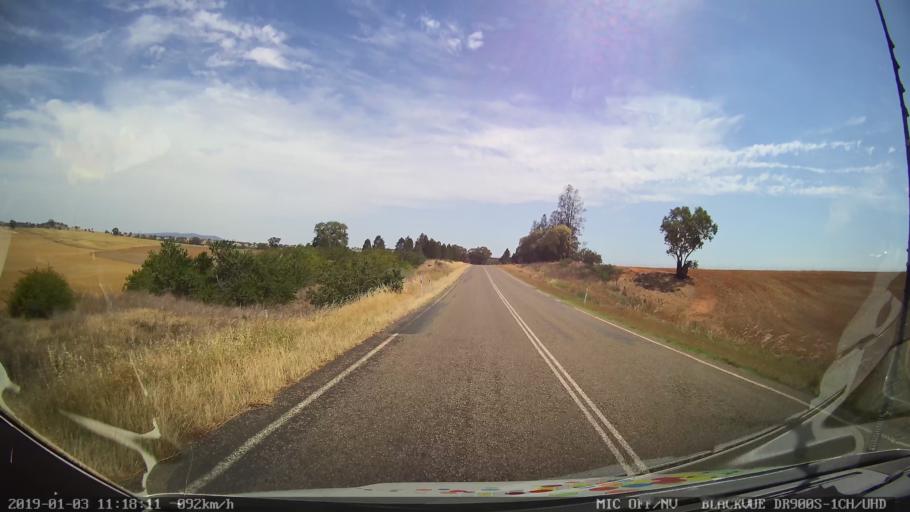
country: AU
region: New South Wales
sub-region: Young
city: Young
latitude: -34.1292
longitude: 148.2636
